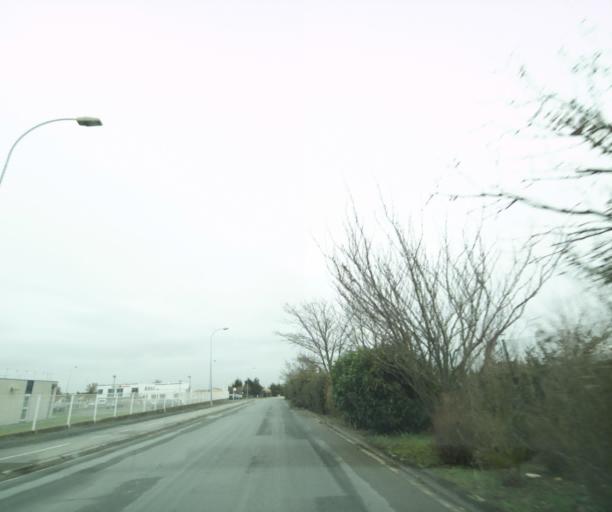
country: FR
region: Poitou-Charentes
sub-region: Departement de la Charente-Maritime
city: Lagord
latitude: 46.1855
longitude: -1.1467
